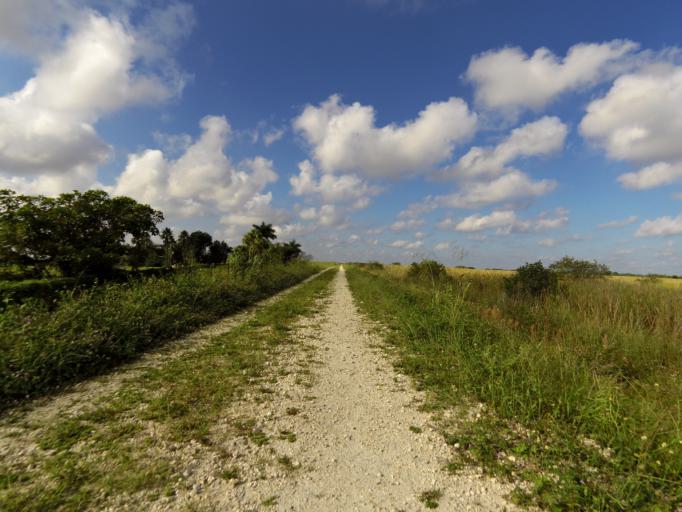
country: US
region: Florida
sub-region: Broward County
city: Weston
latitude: 26.0600
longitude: -80.4479
